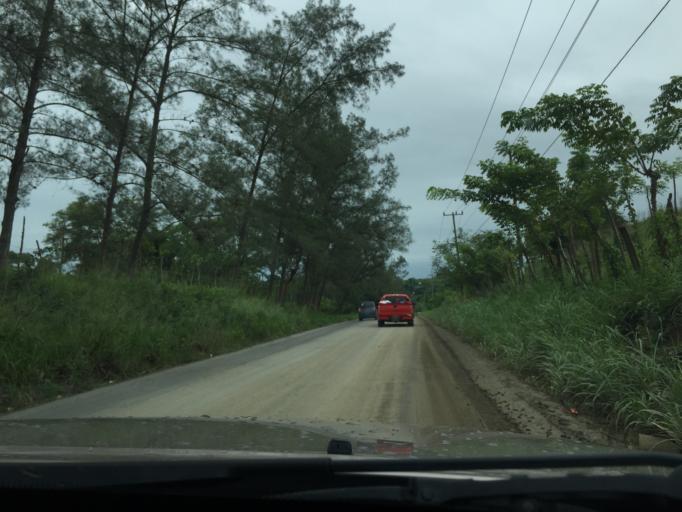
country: MX
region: Veracruz
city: Coatzintla
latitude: 20.4470
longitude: -97.4076
